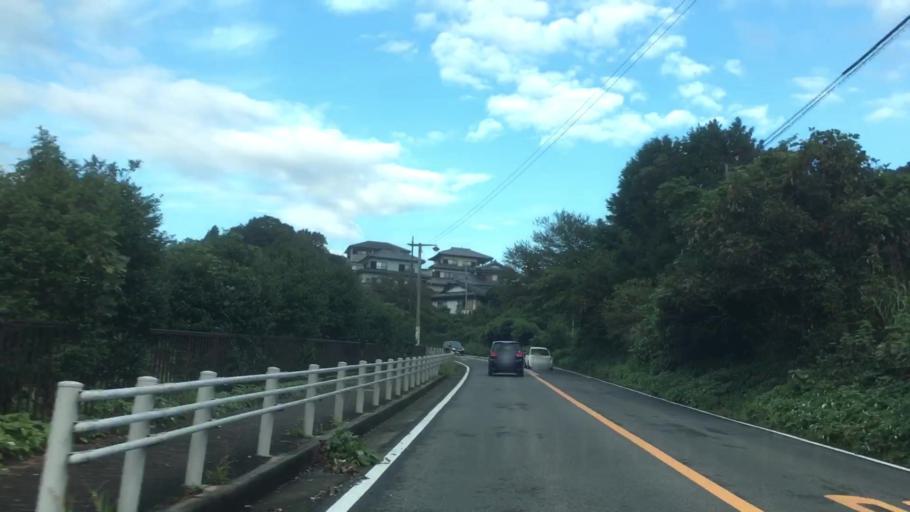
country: JP
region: Nagasaki
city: Togitsu
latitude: 32.9353
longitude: 129.6517
